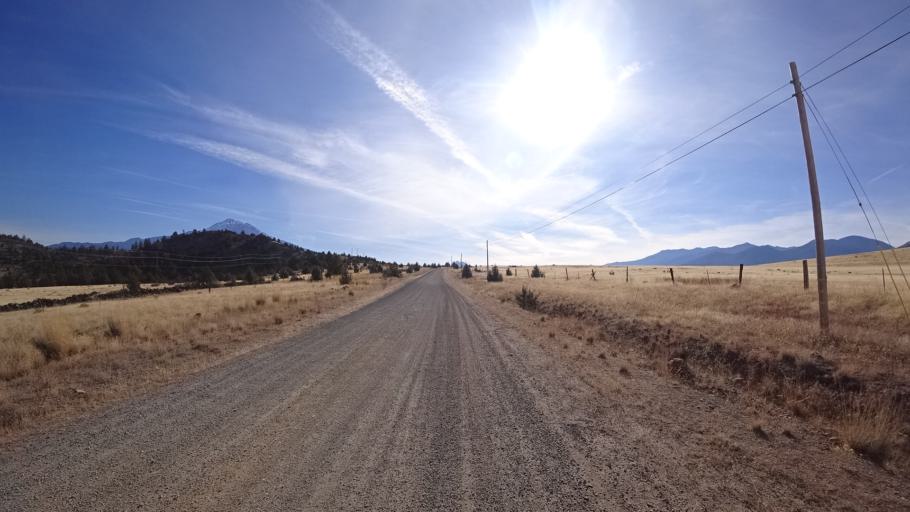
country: US
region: California
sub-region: Siskiyou County
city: Weed
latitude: 41.4947
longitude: -122.4536
